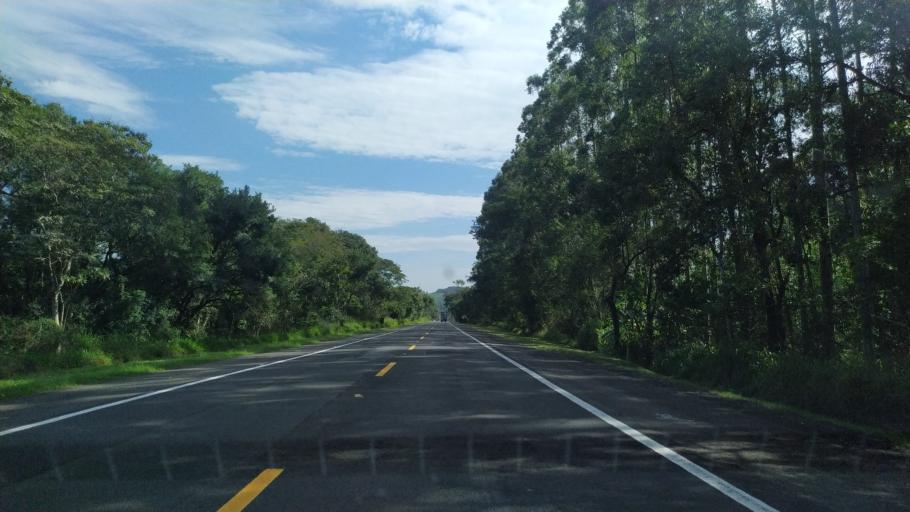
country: BR
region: Parana
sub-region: Ortigueira
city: Ortigueira
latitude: -24.3294
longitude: -50.8461
